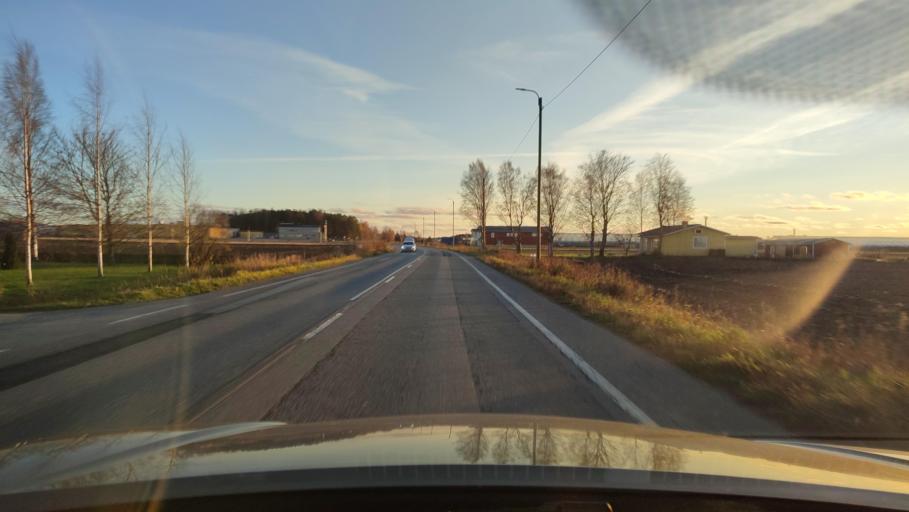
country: FI
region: Ostrobothnia
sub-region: Sydosterbotten
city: Naerpes
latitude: 62.4502
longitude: 21.3526
